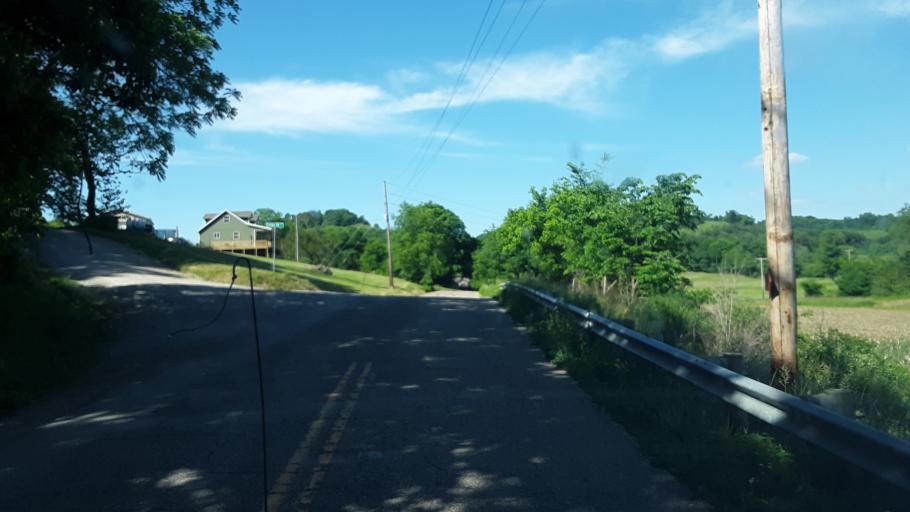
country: US
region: Ohio
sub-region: Tuscarawas County
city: Newcomerstown
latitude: 40.1795
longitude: -81.6423
